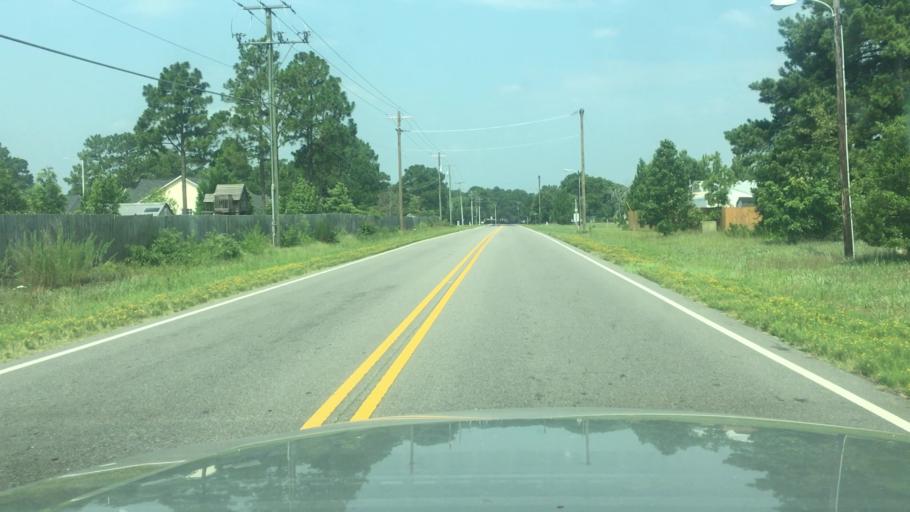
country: US
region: North Carolina
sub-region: Cumberland County
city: Hope Mills
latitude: 35.0001
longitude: -78.9482
